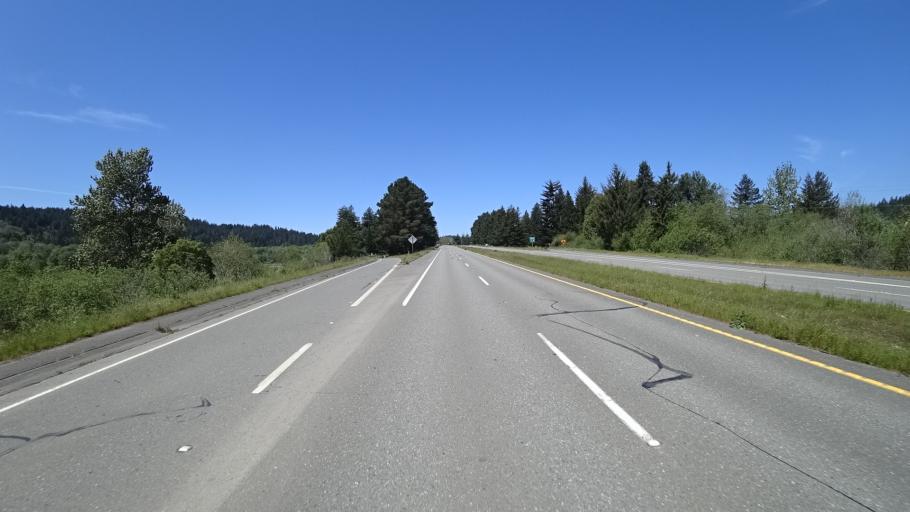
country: US
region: California
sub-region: Humboldt County
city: Blue Lake
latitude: 40.8971
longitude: -124.0189
